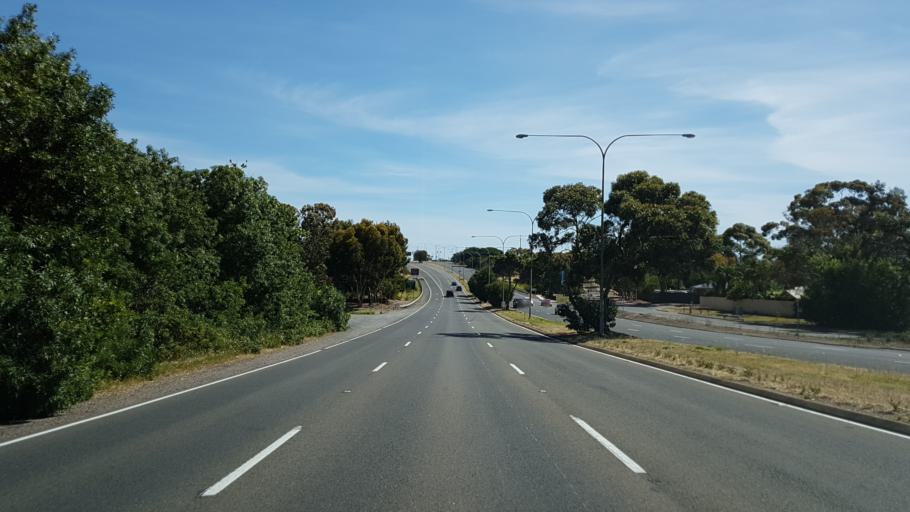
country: AU
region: South Australia
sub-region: Marion
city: Trott Park
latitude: -35.0770
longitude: 138.5493
